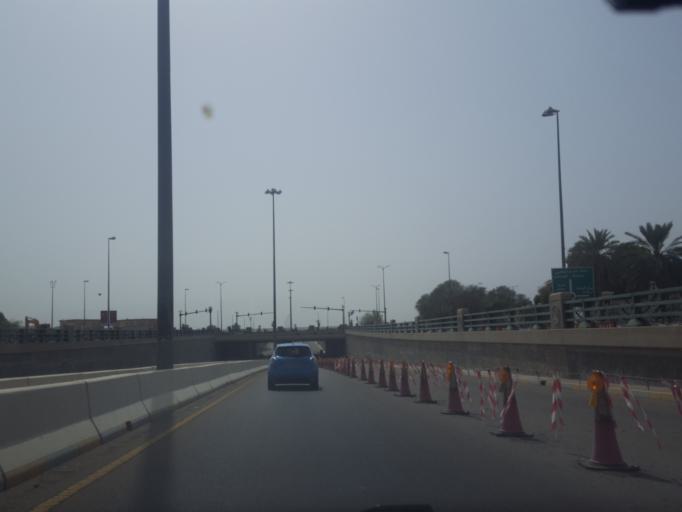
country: AE
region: Abu Dhabi
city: Al Ain
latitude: 24.2057
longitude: 55.7841
